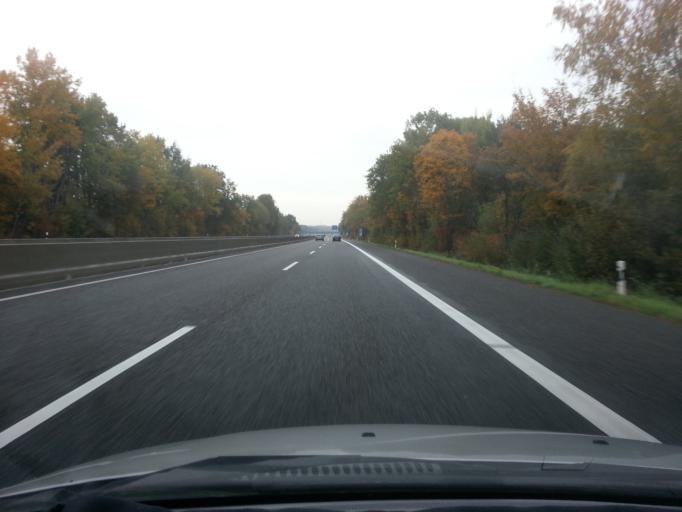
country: DE
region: Hesse
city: Dreieich
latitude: 50.0241
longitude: 8.7104
